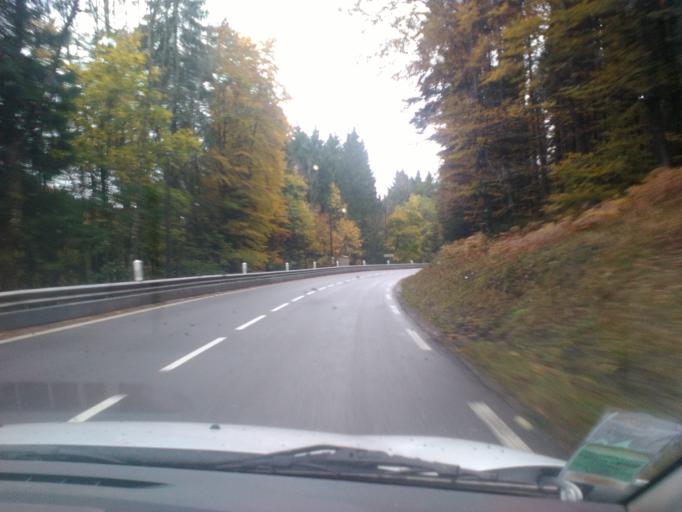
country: FR
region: Lorraine
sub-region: Departement des Vosges
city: Xonrupt-Longemer
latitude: 48.1025
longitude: 6.9056
